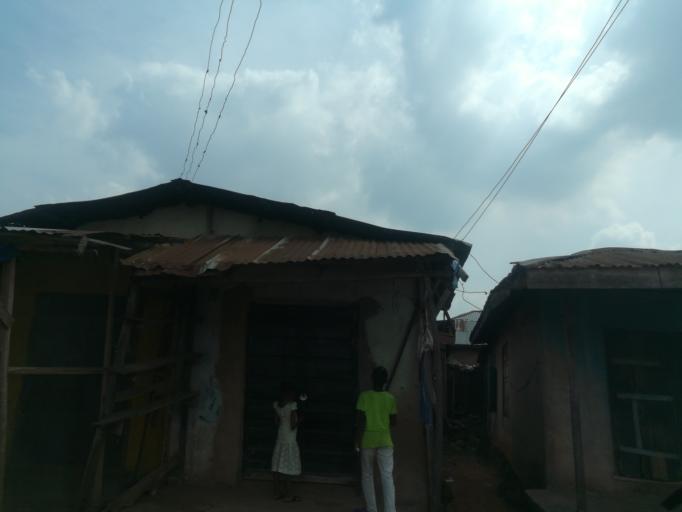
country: NG
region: Oyo
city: Ibadan
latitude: 7.3900
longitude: 3.9075
